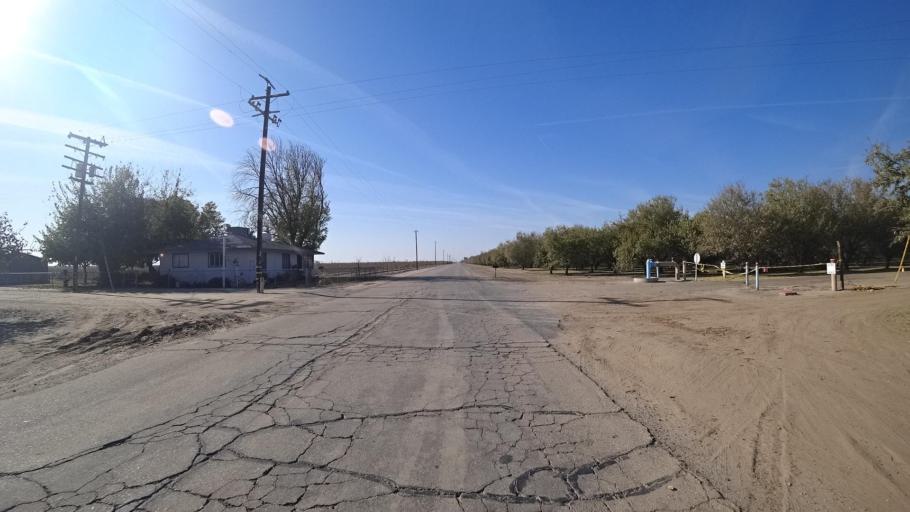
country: US
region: California
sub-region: Kern County
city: Wasco
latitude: 35.6670
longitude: -119.3660
